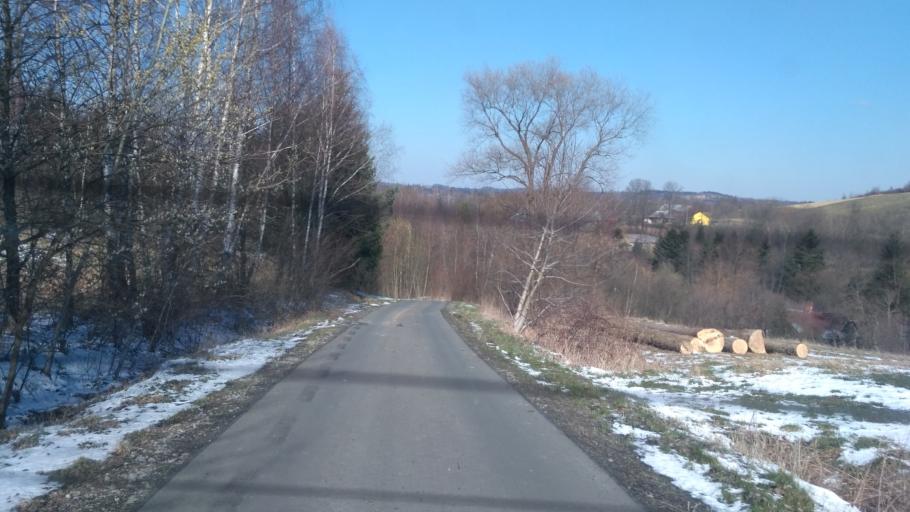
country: PL
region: Subcarpathian Voivodeship
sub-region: Powiat strzyzowski
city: Gwoznica Gorna
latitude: 49.8241
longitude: 22.0069
